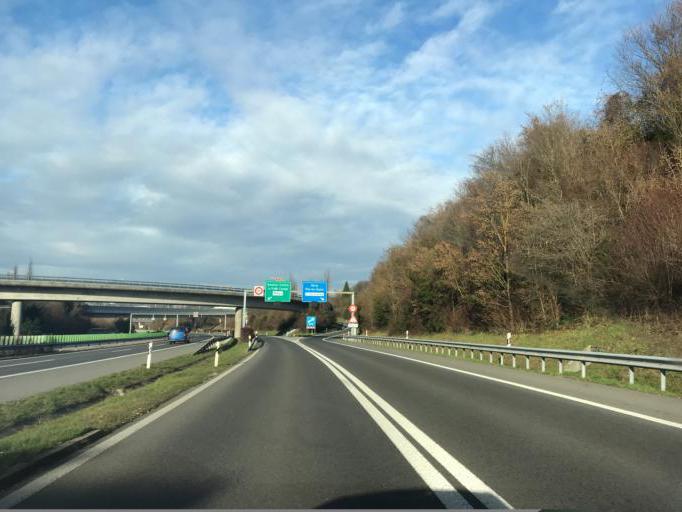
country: CH
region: Geneva
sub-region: Geneva
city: Plan-les-Ouates
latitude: 46.1584
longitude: 6.1016
